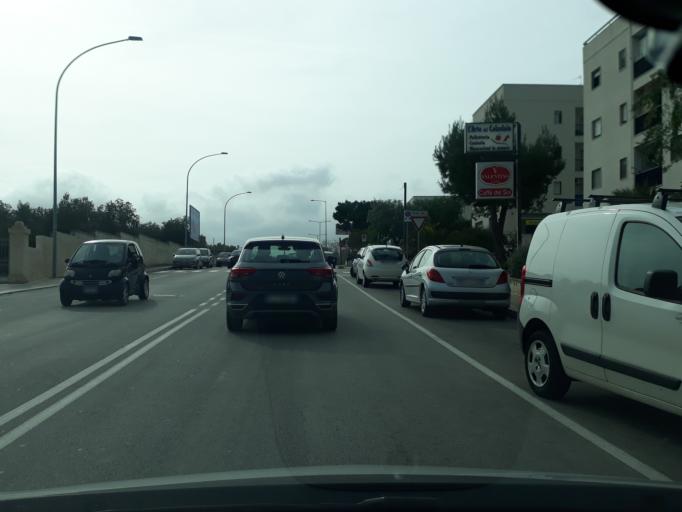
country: IT
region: Apulia
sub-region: Provincia di Bari
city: Monopoli
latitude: 40.9447
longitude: 17.2928
